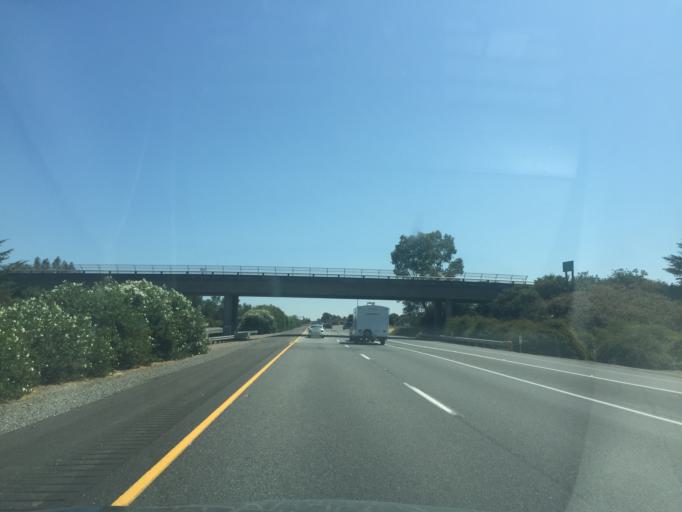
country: US
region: California
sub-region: Tehama County
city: Corning
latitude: 39.9289
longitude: -122.2005
